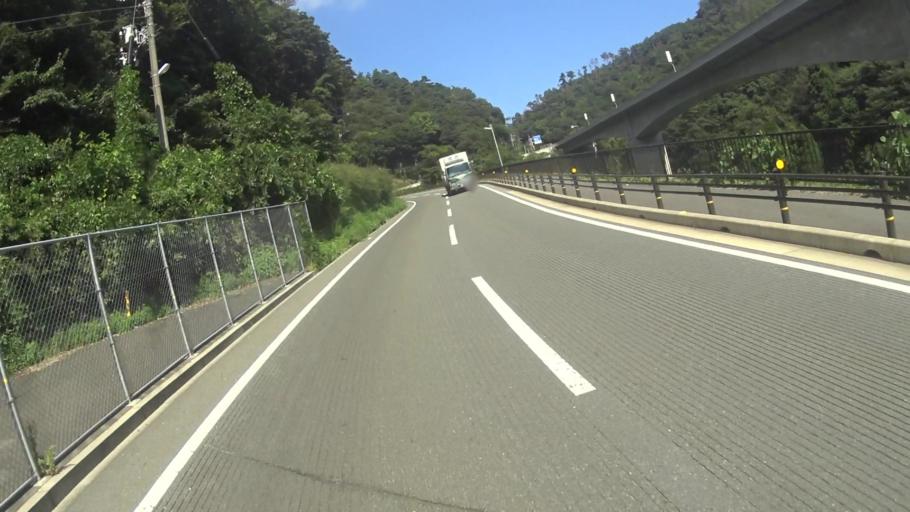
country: JP
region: Kyoto
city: Miyazu
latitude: 35.6811
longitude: 135.2863
